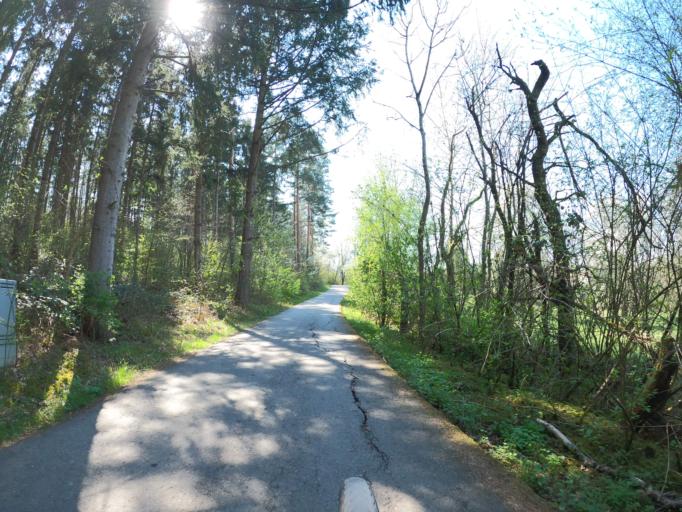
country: DE
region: Baden-Wuerttemberg
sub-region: Tuebingen Region
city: Wannweil
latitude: 48.4819
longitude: 9.1573
